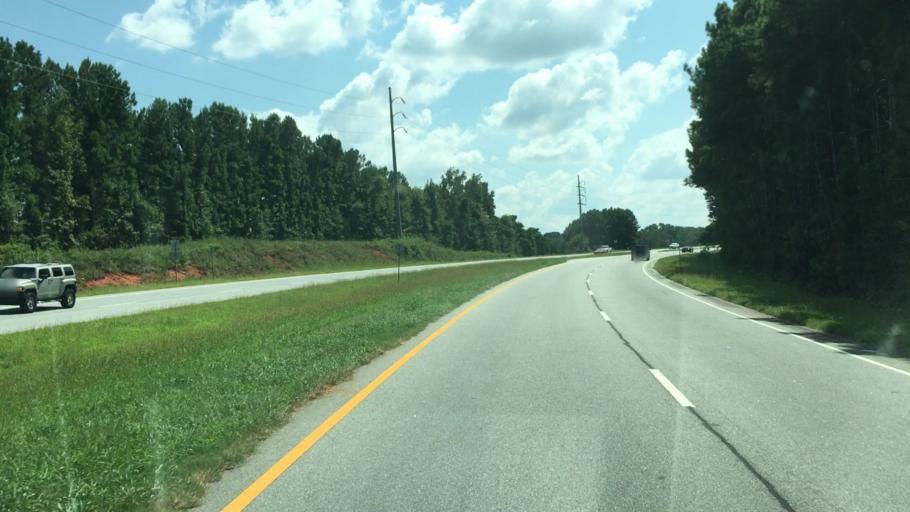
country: US
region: Georgia
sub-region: Morgan County
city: Madison
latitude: 33.5790
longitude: -83.4486
